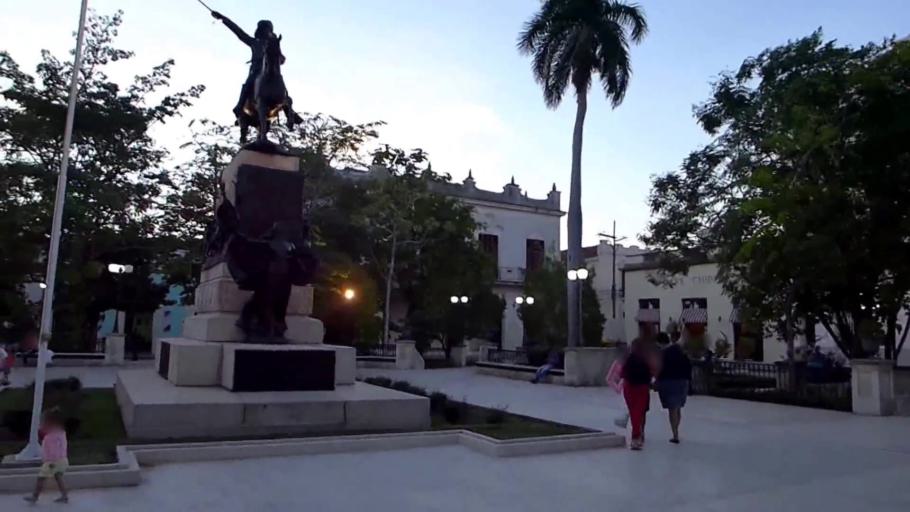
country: CU
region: Camaguey
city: Camaguey
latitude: 21.3793
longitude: -77.9185
